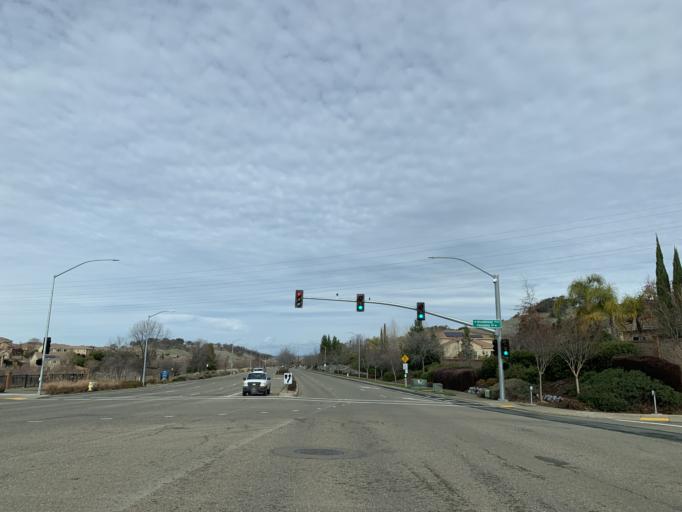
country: US
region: California
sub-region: El Dorado County
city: El Dorado Hills
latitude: 38.6554
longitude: -121.0923
